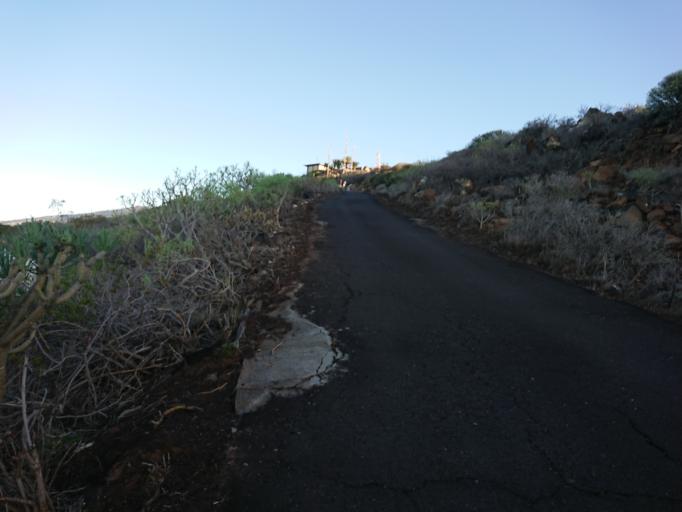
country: ES
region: Canary Islands
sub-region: Provincia de Santa Cruz de Tenerife
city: Tazacorte
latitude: 28.6613
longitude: -17.9433
